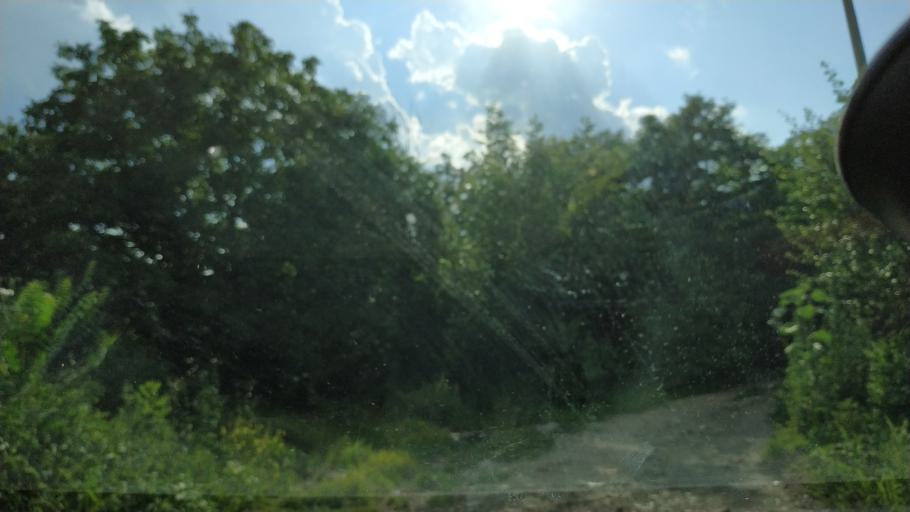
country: RS
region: Central Serbia
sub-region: Nisavski Okrug
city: Aleksinac
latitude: 43.6021
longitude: 21.6916
